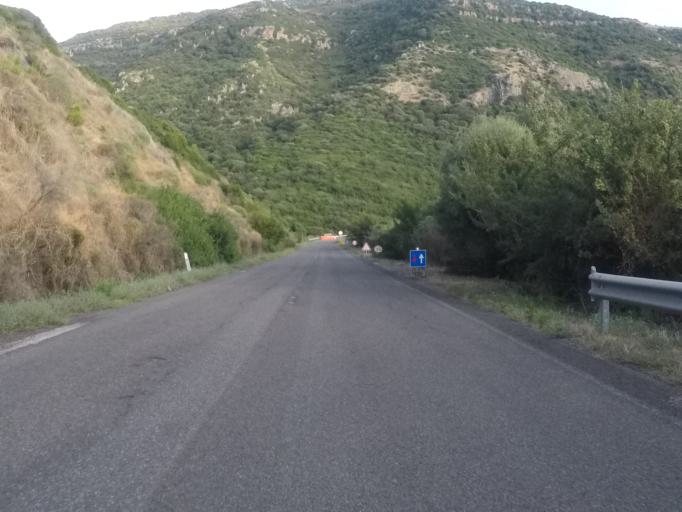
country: IT
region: Sardinia
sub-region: Provincia di Oristano
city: Montresta
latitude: 40.4077
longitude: 8.4116
